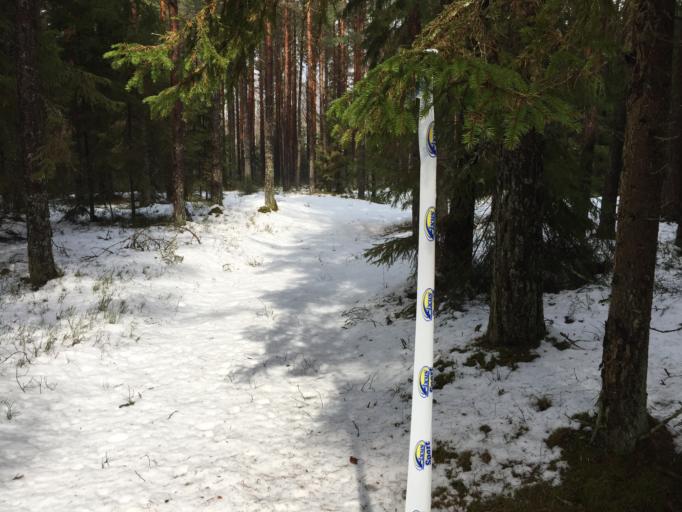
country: EE
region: Saare
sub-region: Kuressaare linn
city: Kuressaare
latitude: 58.3964
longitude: 22.1613
